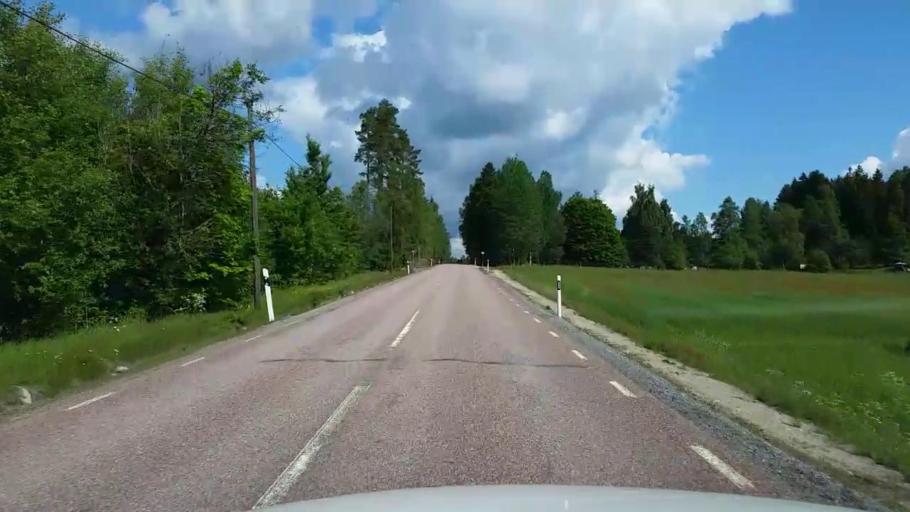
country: SE
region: Vaestmanland
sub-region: Kopings Kommun
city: Kolsva
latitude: 59.6886
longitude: 15.7743
